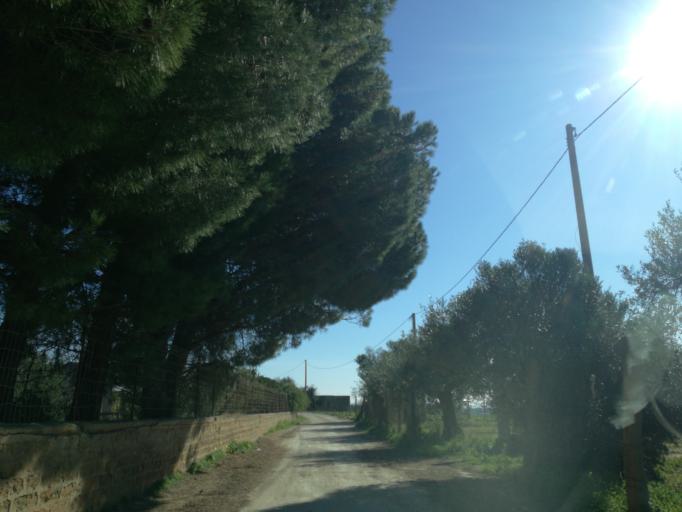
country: IT
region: Sicily
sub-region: Provincia di Caltanissetta
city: Niscemi
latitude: 37.0583
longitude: 14.3586
